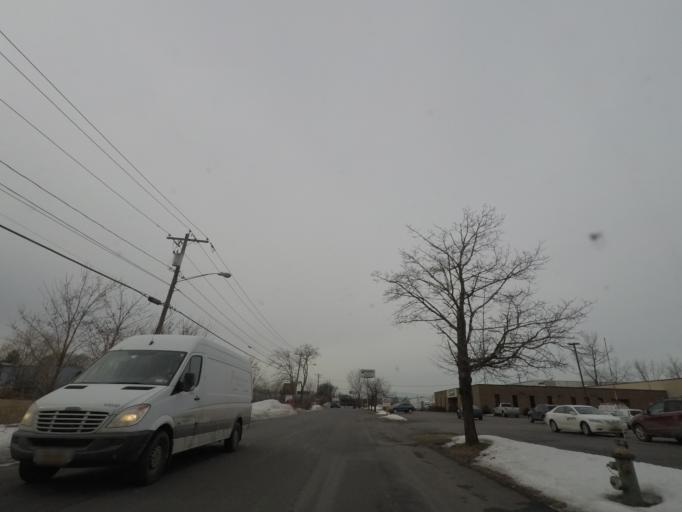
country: US
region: New York
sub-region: Albany County
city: West Albany
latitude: 42.6781
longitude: -73.7758
